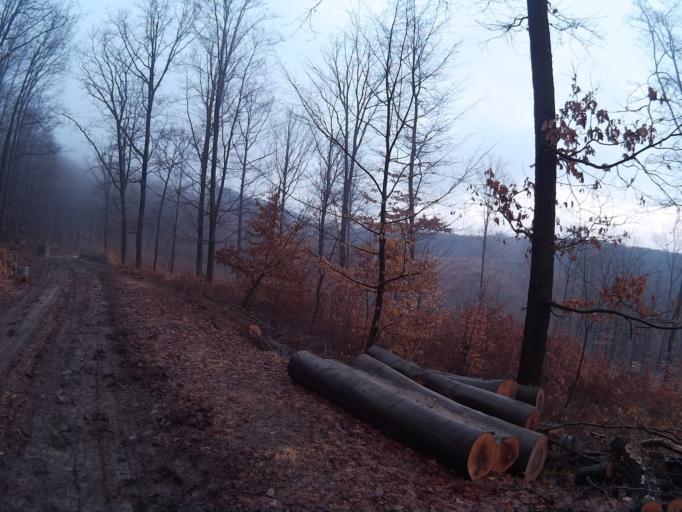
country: HU
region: Borsod-Abauj-Zemplen
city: Satoraljaujhely
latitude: 48.4223
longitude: 21.5705
